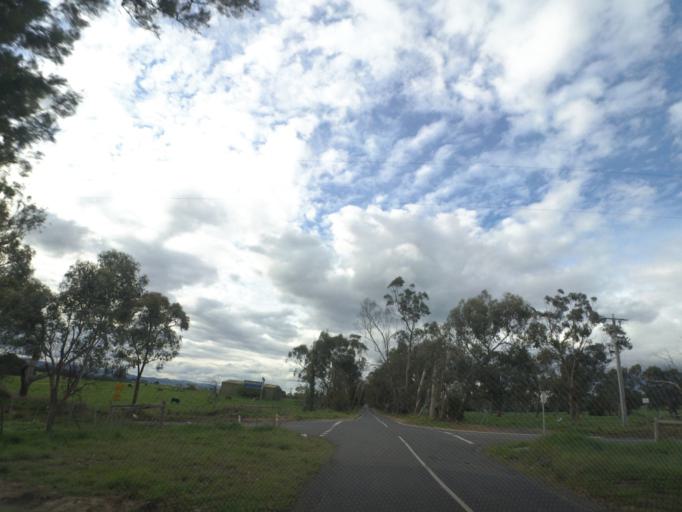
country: AU
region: Victoria
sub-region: Yarra Ranges
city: Mount Evelyn
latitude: -37.7395
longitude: 145.4132
